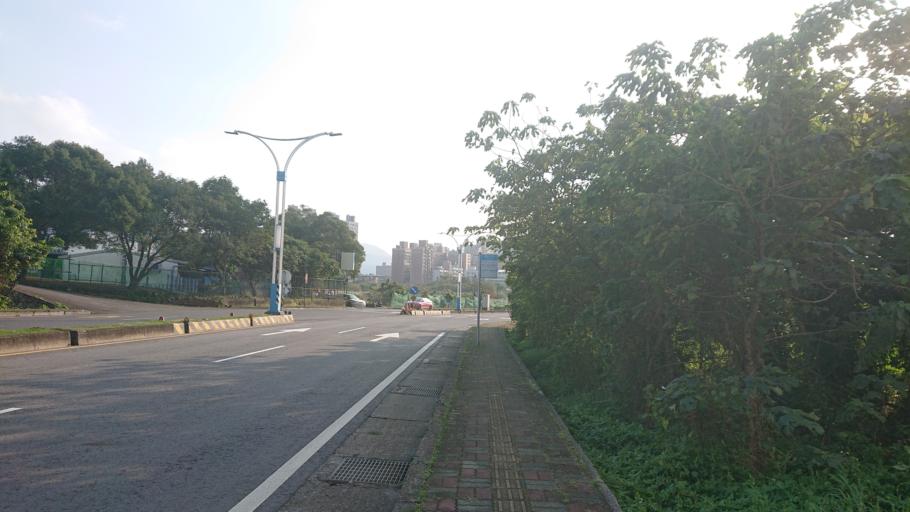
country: TW
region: Taipei
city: Taipei
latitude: 25.1891
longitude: 121.4262
